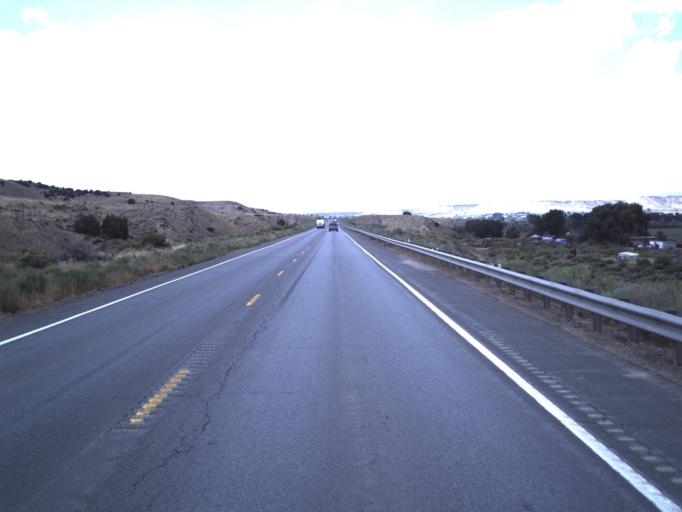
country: US
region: Utah
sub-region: Duchesne County
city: Duchesne
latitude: 40.1621
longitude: -110.2756
